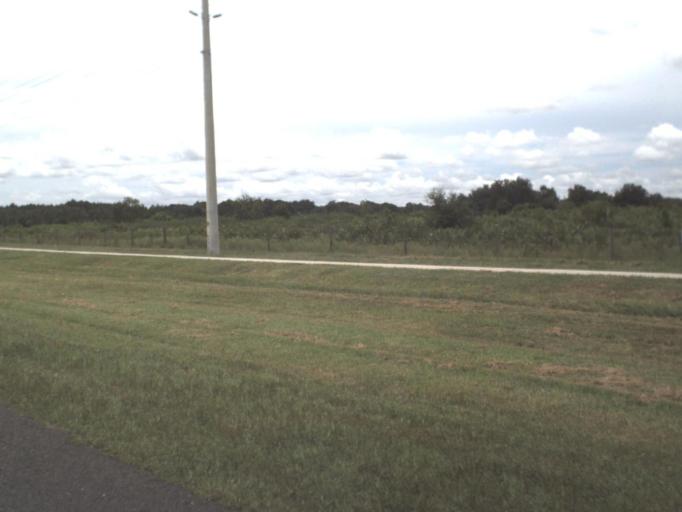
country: US
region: Florida
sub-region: Hillsborough County
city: Pebble Creek
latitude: 28.1936
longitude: -82.3357
